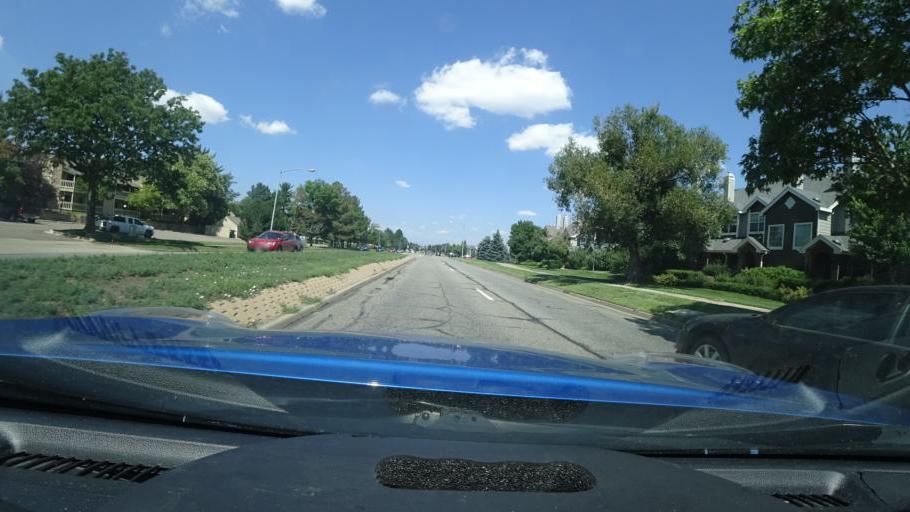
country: US
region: Colorado
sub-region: Arapahoe County
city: Glendale
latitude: 39.7088
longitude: -104.8883
